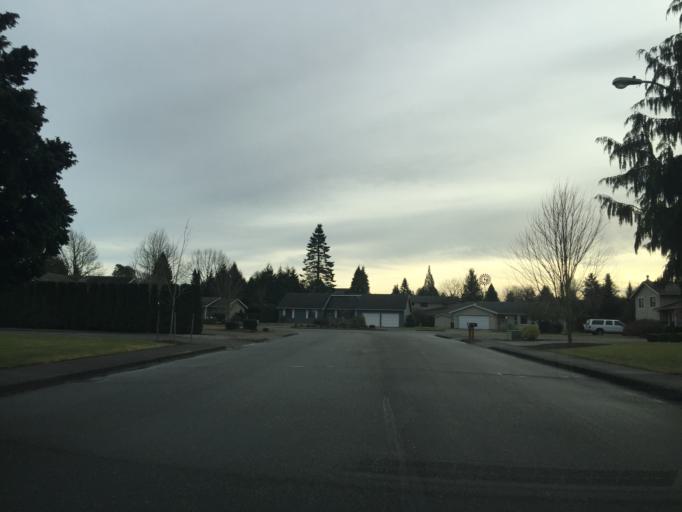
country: US
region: Washington
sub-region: Whatcom County
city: Lynden
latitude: 48.9545
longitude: -122.4398
